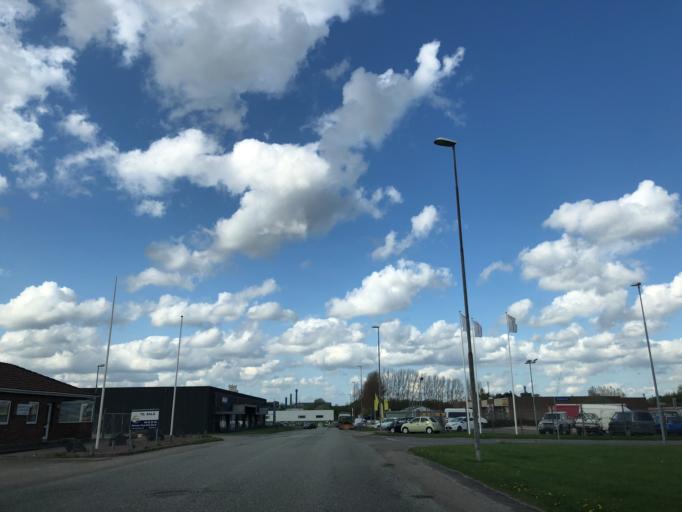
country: DK
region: Zealand
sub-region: Ringsted Kommune
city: Ringsted
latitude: 55.4268
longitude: 11.7904
